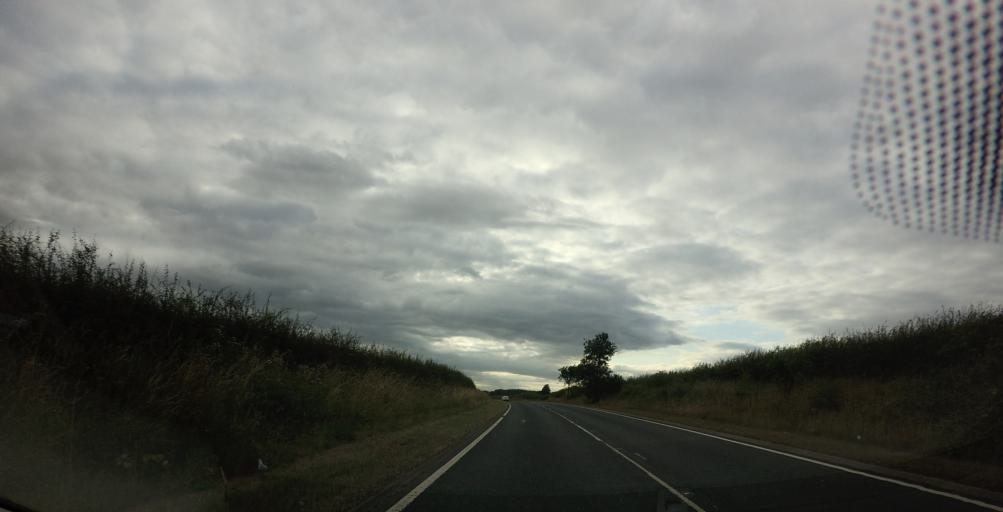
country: GB
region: England
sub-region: City and Borough of Leeds
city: Walton
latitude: 54.0055
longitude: -1.3362
